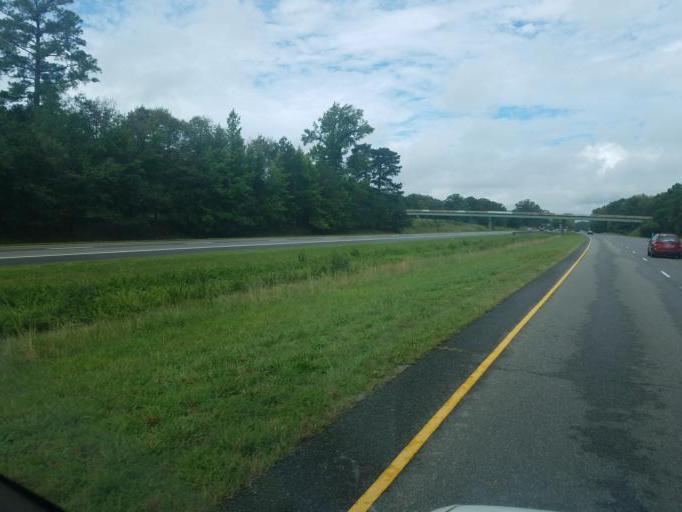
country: US
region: Virginia
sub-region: Henrico County
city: Sandston
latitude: 37.5233
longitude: -77.2777
